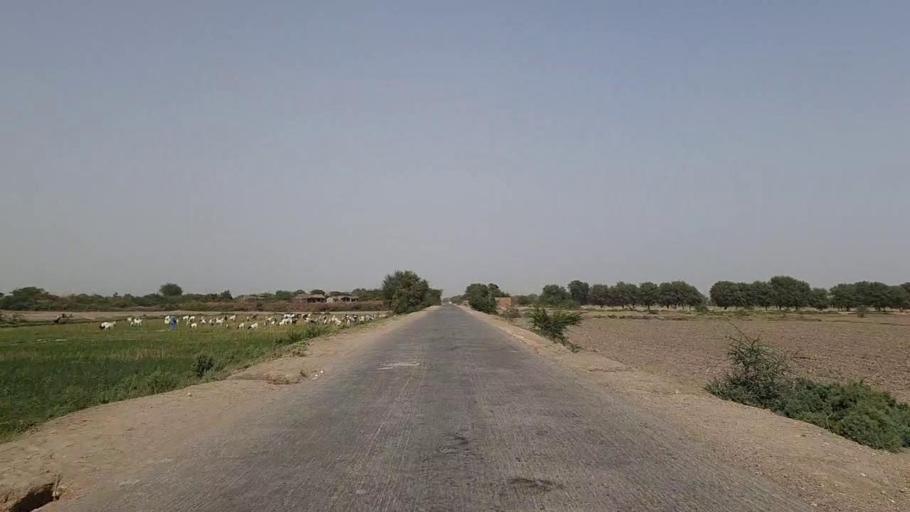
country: PK
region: Sindh
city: Tando Bago
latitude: 24.9101
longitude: 69.0927
